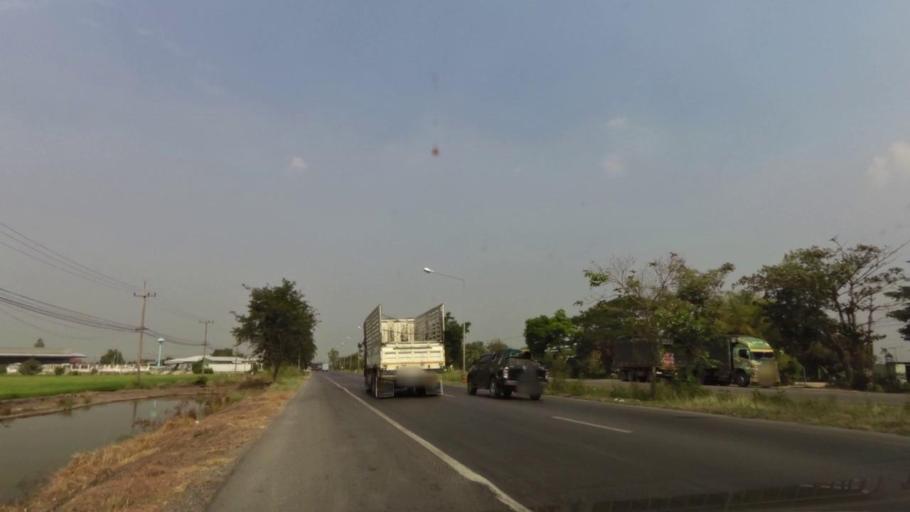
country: TH
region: Phra Nakhon Si Ayutthaya
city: Phra Nakhon Si Ayutthaya
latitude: 14.3130
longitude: 100.5277
